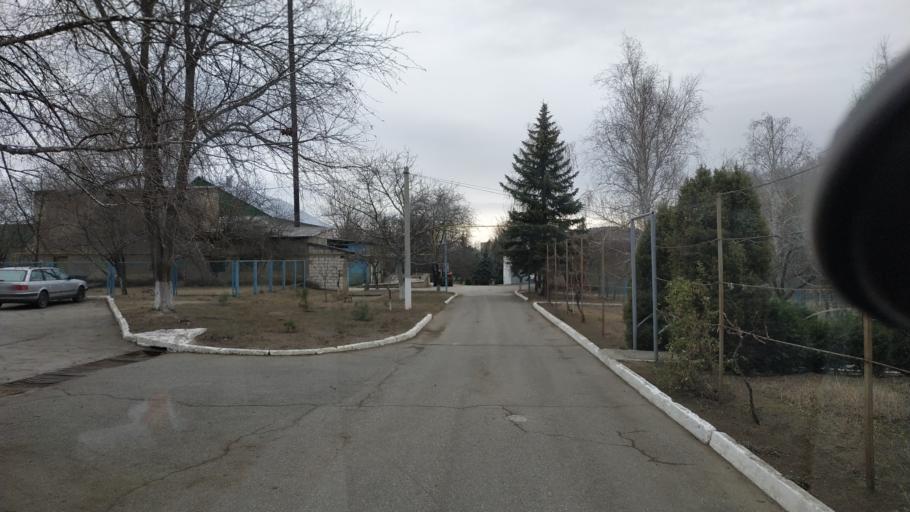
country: MD
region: Telenesti
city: Cocieri
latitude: 47.2930
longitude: 29.1189
